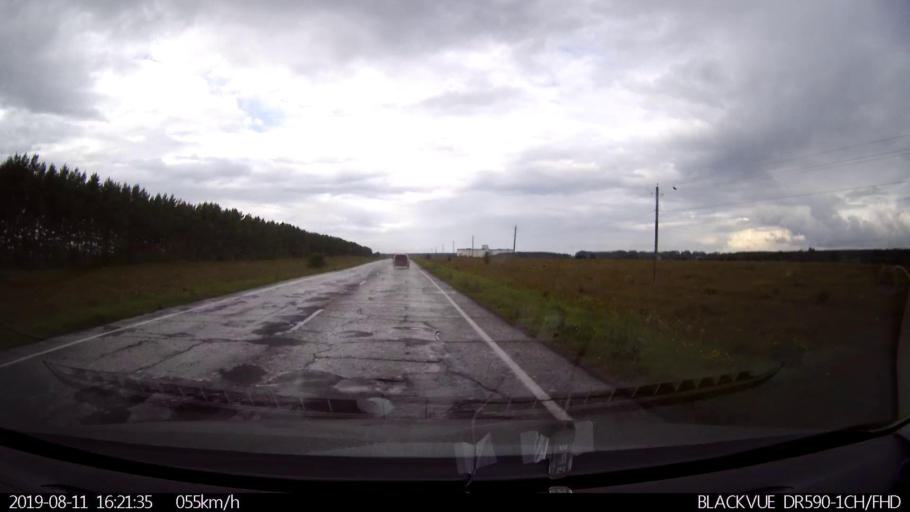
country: RU
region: Ulyanovsk
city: Mayna
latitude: 54.0810
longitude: 47.5972
